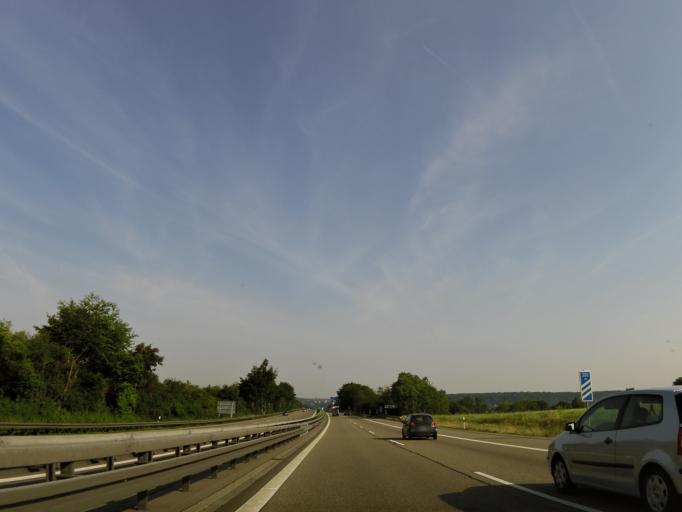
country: DE
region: Baden-Wuerttemberg
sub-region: Karlsruhe Region
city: Niefern-Oschelbronn
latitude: 48.9027
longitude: 8.7786
